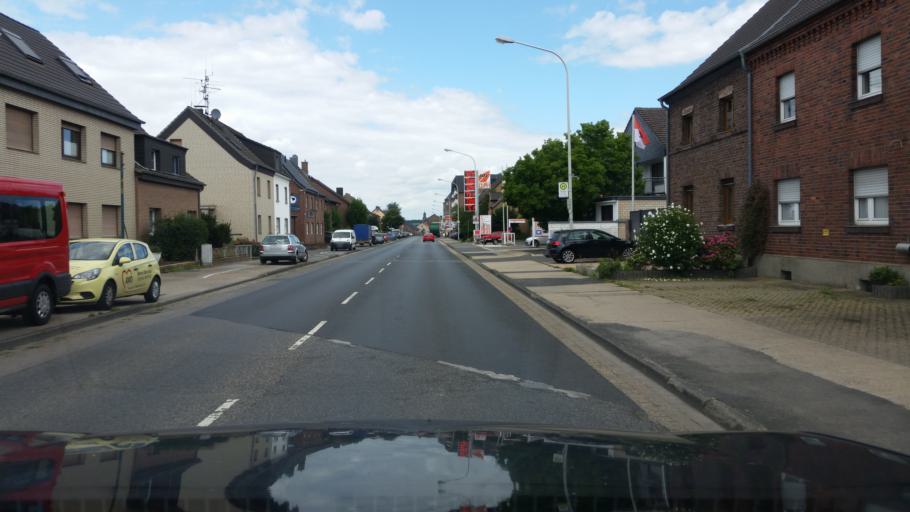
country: DE
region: North Rhine-Westphalia
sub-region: Regierungsbezirk Koln
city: Weilerswist
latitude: 50.7494
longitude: 6.8379
